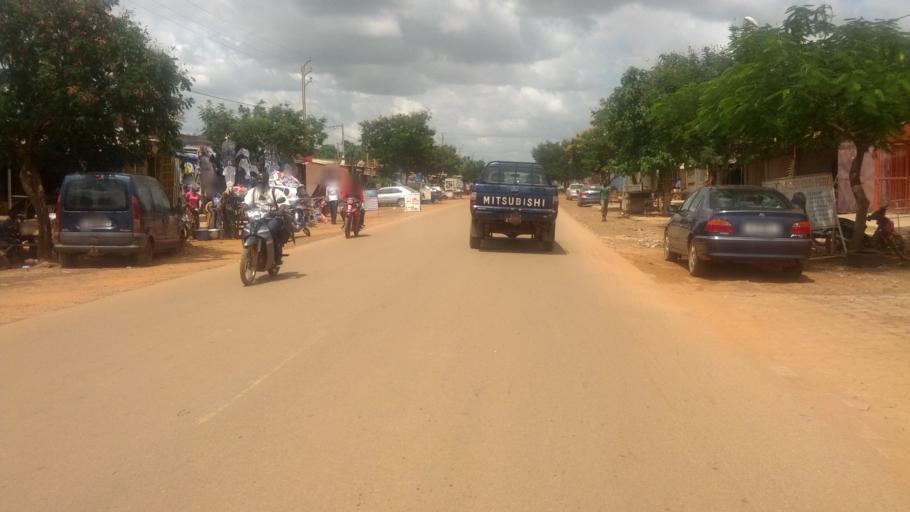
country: BF
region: Centre
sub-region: Kadiogo Province
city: Ouagadougou
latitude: 12.3491
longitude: -1.5018
